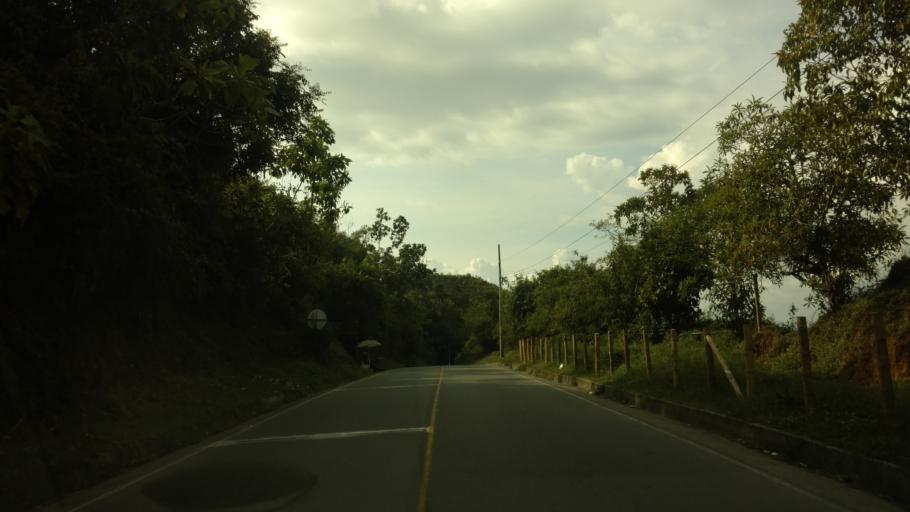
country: CO
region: Caldas
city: Neira
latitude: 5.1577
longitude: -75.5143
